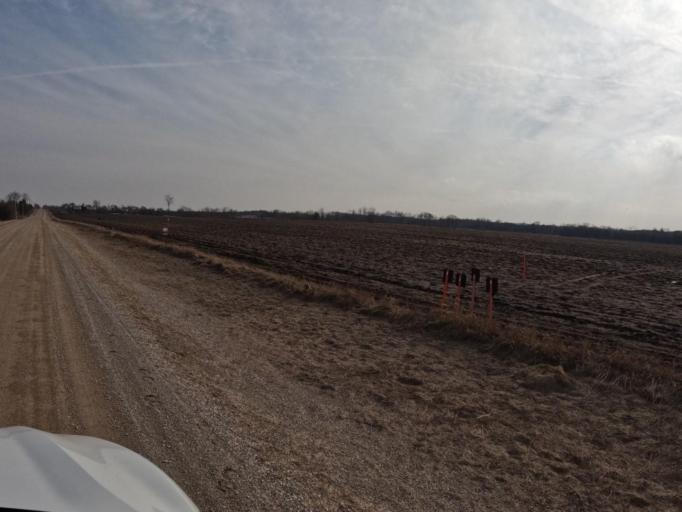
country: CA
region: Ontario
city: Orangeville
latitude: 43.9097
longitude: -80.2700
